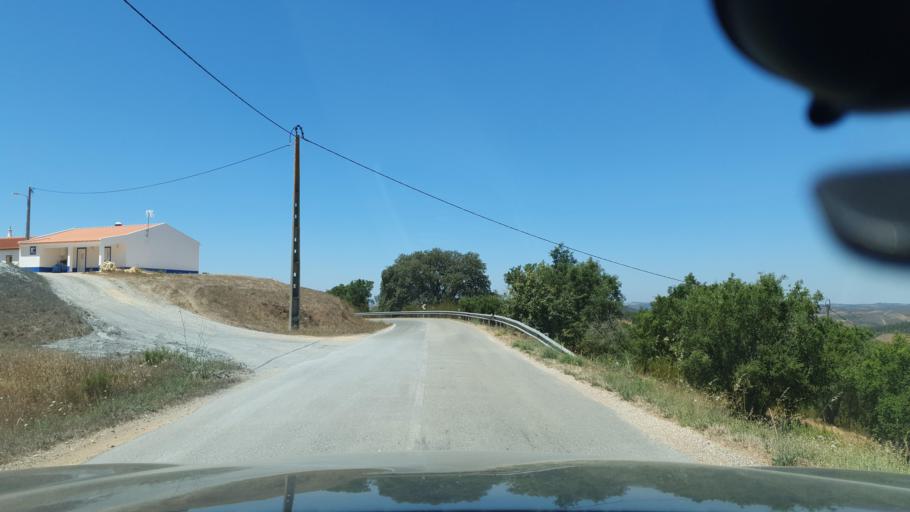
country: PT
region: Beja
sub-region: Odemira
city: Odemira
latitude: 37.5535
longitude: -8.4319
